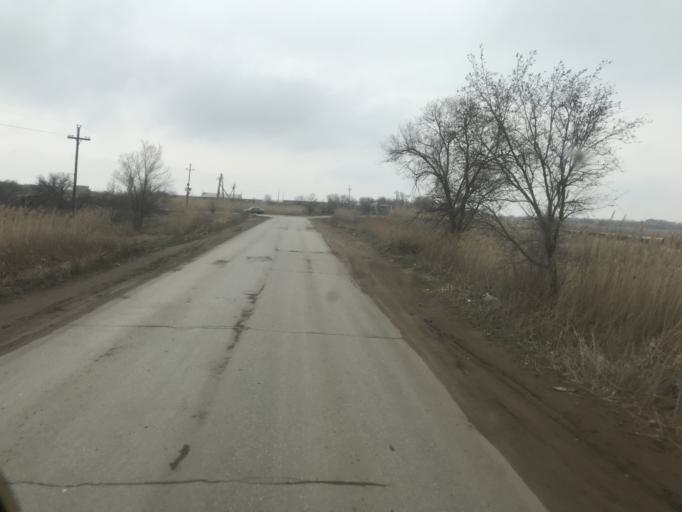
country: RU
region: Volgograd
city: Svetlyy Yar
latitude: 48.5286
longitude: 44.6107
